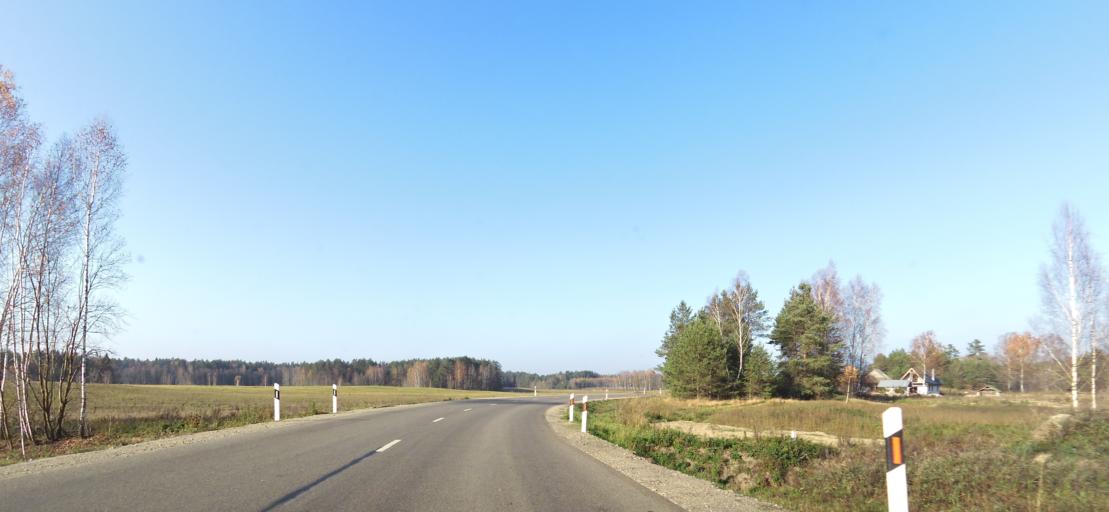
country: LT
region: Vilnius County
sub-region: Trakai
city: Rudiskes
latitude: 54.5081
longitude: 24.8668
